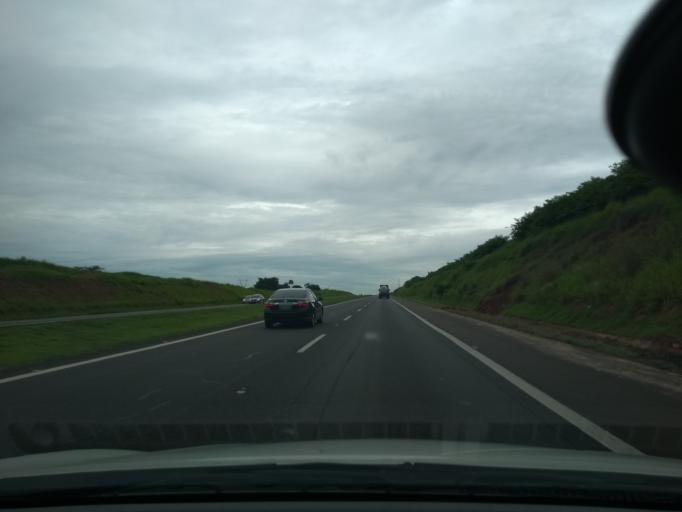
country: BR
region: Sao Paulo
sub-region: Iracemapolis
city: Iracemapolis
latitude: -22.6319
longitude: -47.4559
